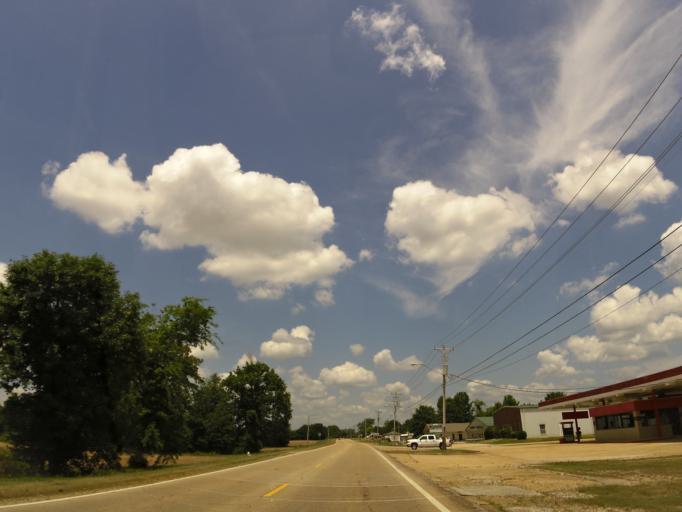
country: US
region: Mississippi
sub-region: Lee County
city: Tupelo
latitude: 34.2748
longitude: -88.6805
